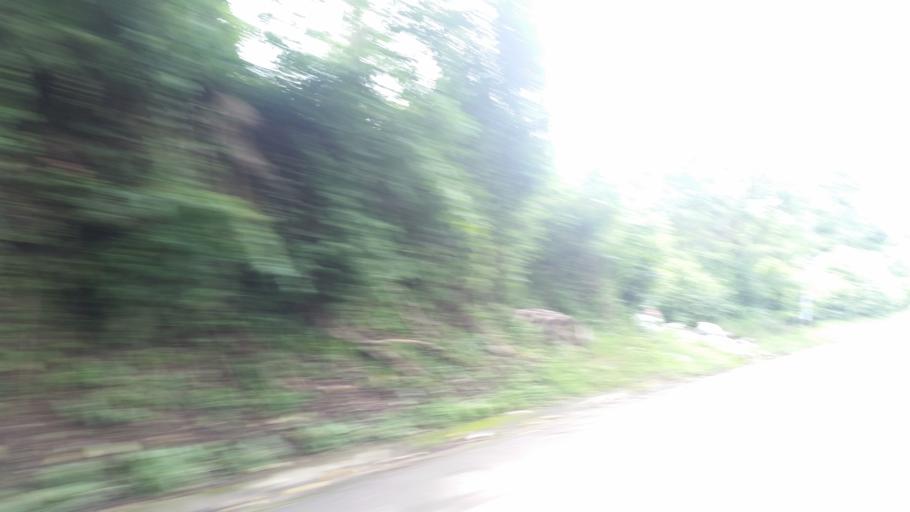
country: CO
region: Magdalena
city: Santa Marta
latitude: 11.2814
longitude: -73.9125
